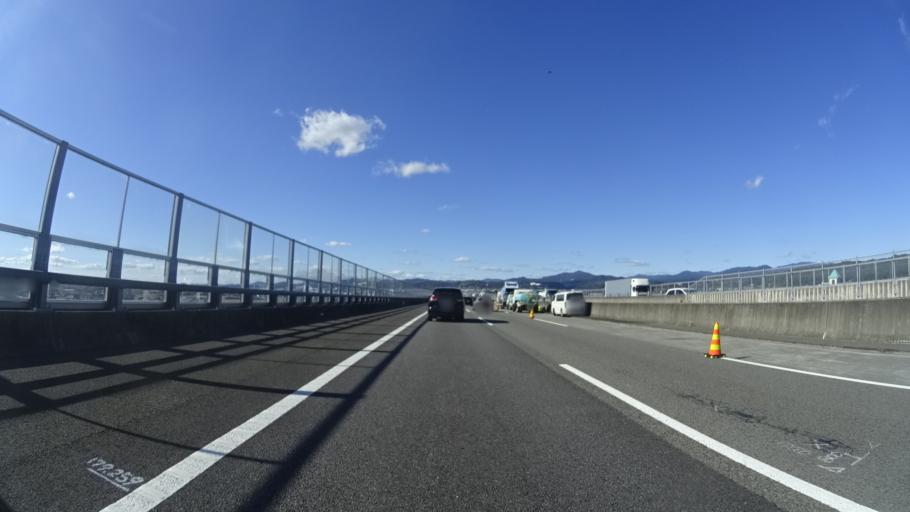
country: JP
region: Shizuoka
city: Hamakita
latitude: 34.8273
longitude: 137.8468
